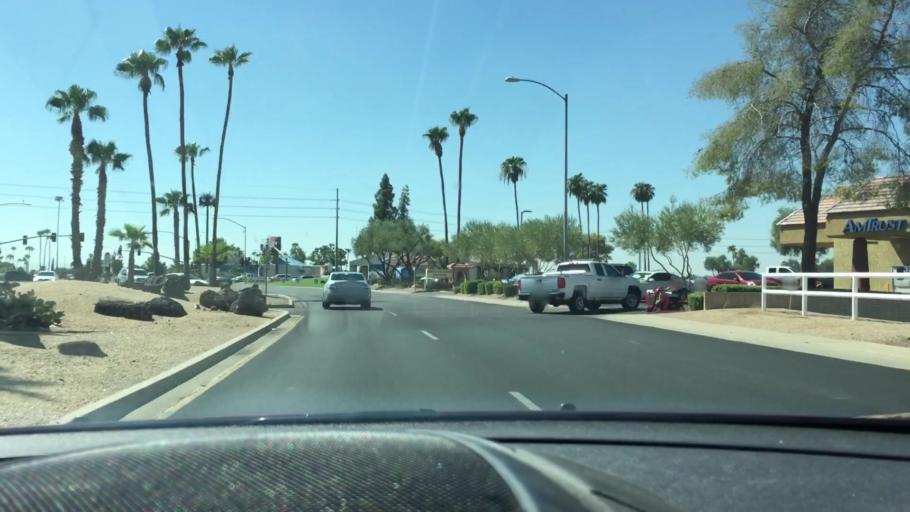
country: US
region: Arizona
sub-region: Maricopa County
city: El Mirage
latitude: 33.6395
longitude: -112.2896
